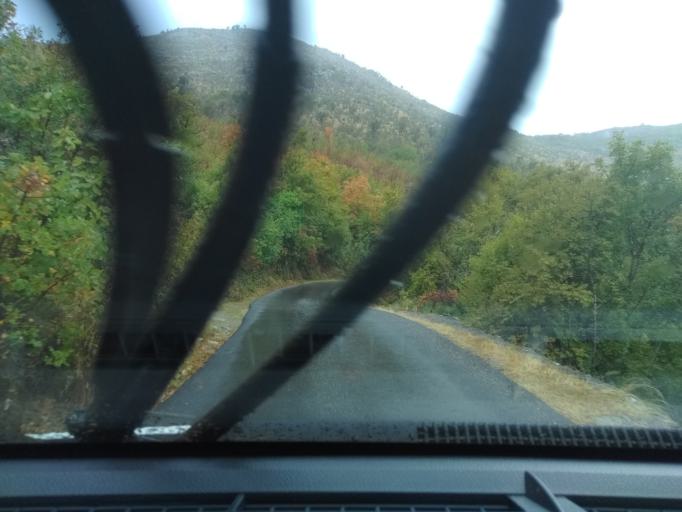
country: ME
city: Stari Bar
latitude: 42.1814
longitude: 19.1782
